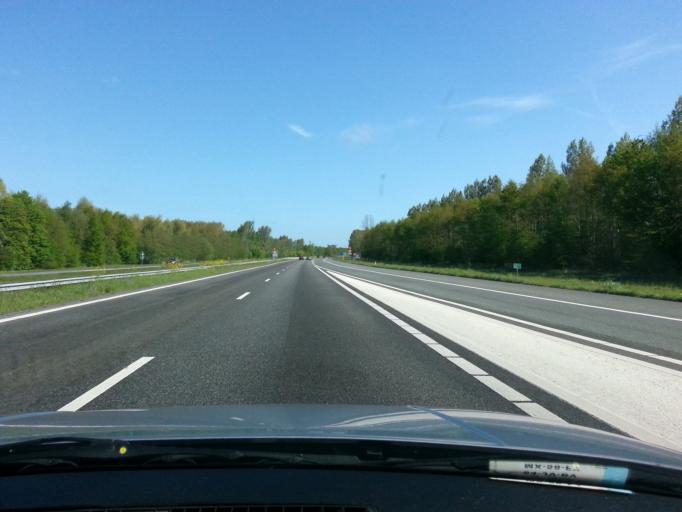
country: NL
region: Flevoland
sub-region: Gemeente Lelystad
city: Lelystad
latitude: 52.5506
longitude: 5.5311
